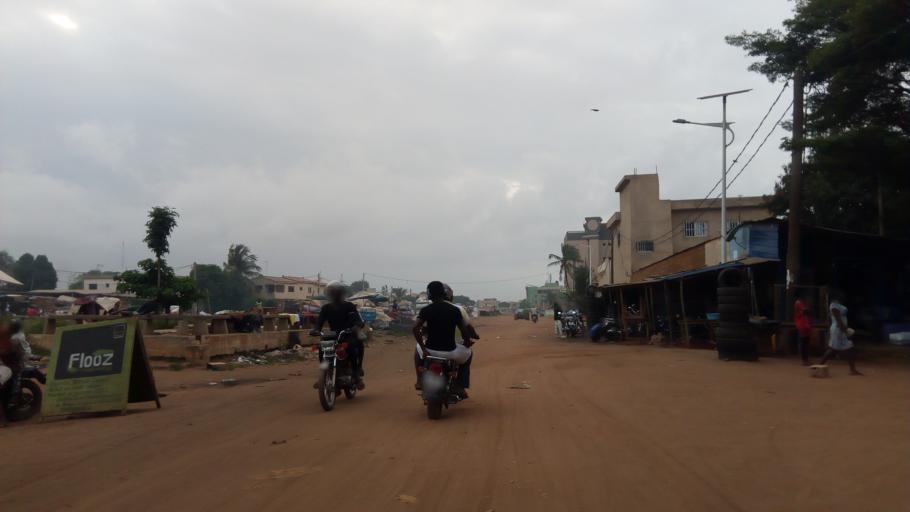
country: TG
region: Maritime
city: Lome
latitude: 6.1644
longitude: 1.2053
